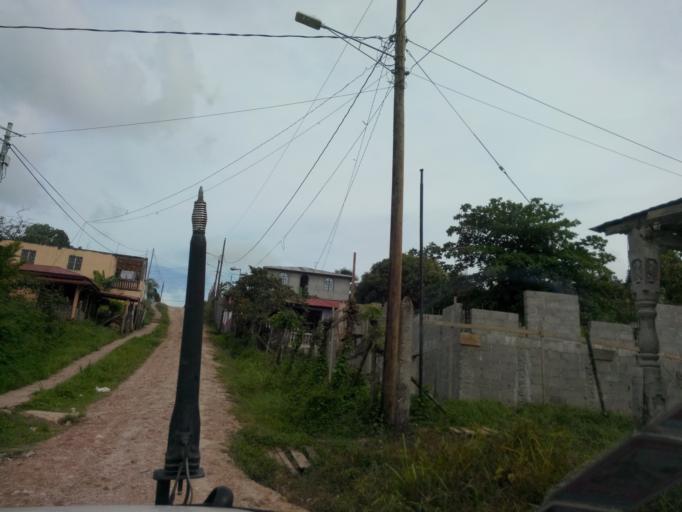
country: NI
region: Atlantico Sur
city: Bluefields
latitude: 12.0014
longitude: -83.7680
